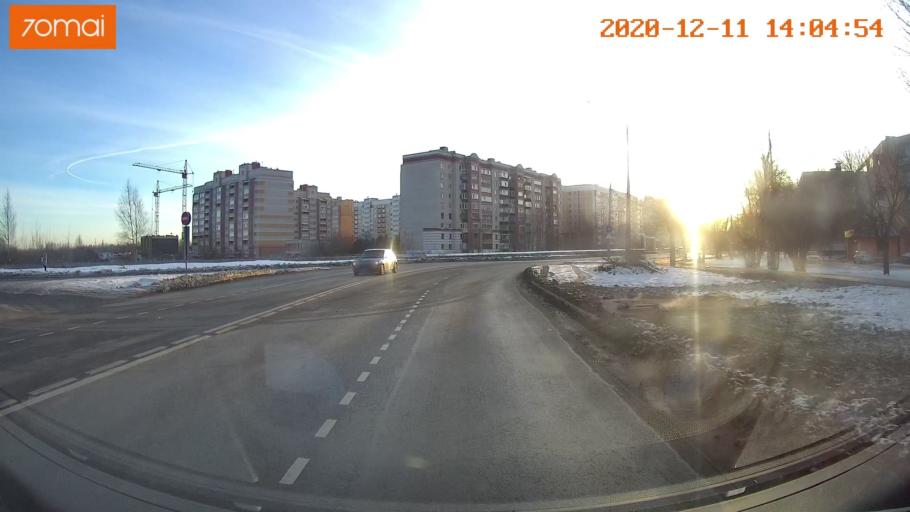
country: RU
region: Kostroma
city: Oktyabr'skiy
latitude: 57.7508
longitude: 41.0163
